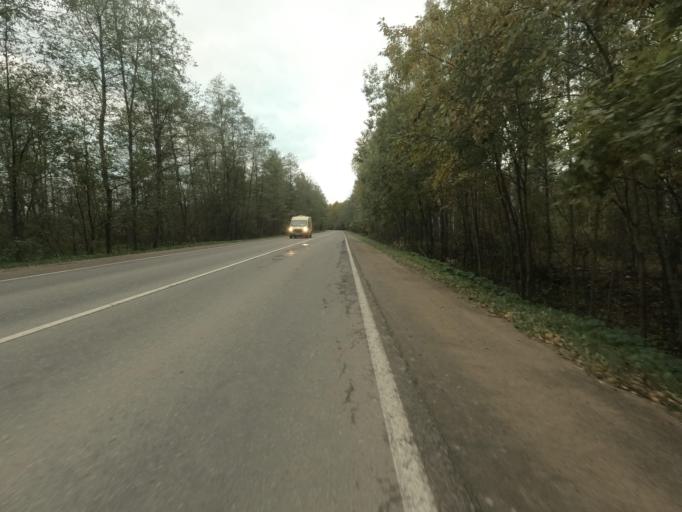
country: RU
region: Leningrad
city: Pavlovo
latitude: 59.7993
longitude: 30.9433
